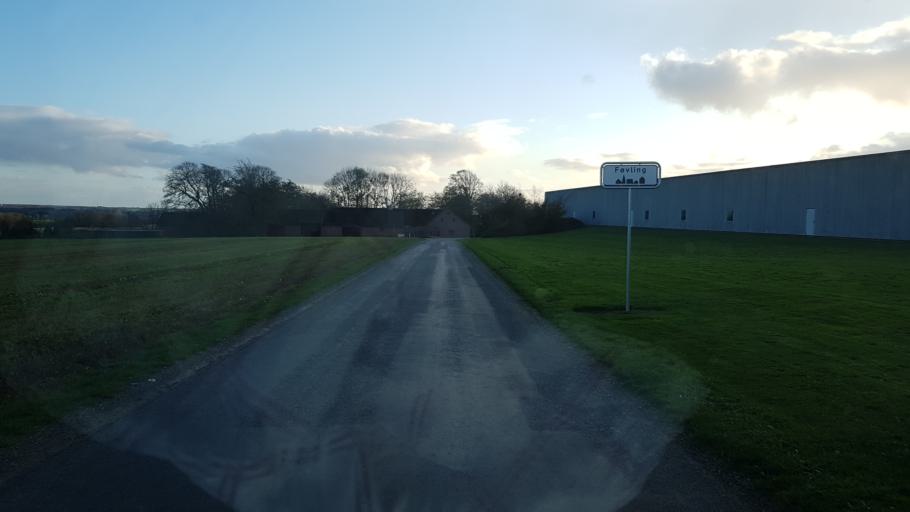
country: DK
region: South Denmark
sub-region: Vejen Kommune
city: Holsted
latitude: 55.4534
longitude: 8.9423
